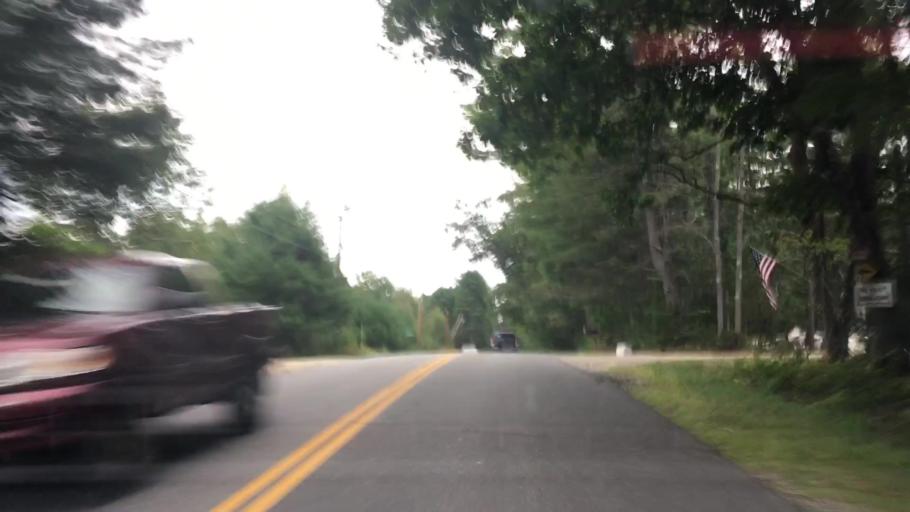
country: US
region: Maine
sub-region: Cumberland County
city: Freeport
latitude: 43.8807
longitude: -70.1606
